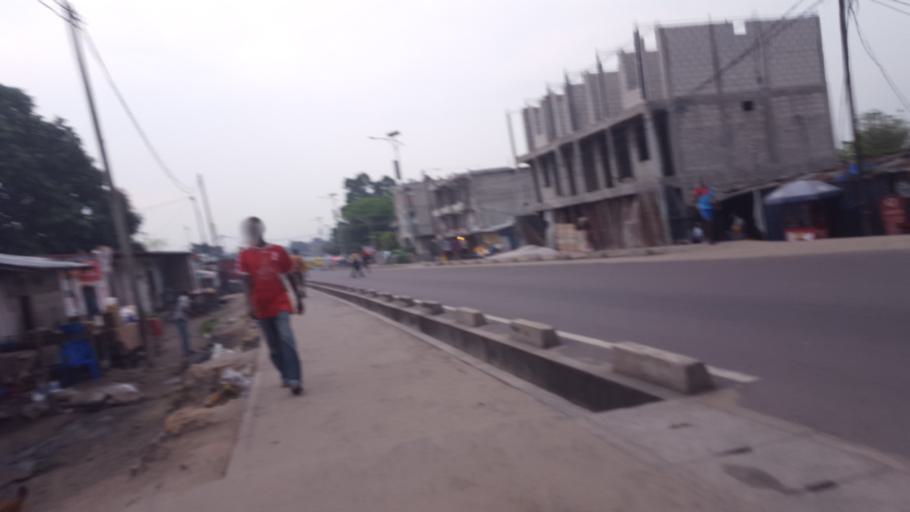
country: CD
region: Kinshasa
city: Masina
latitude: -4.3849
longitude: 15.3566
